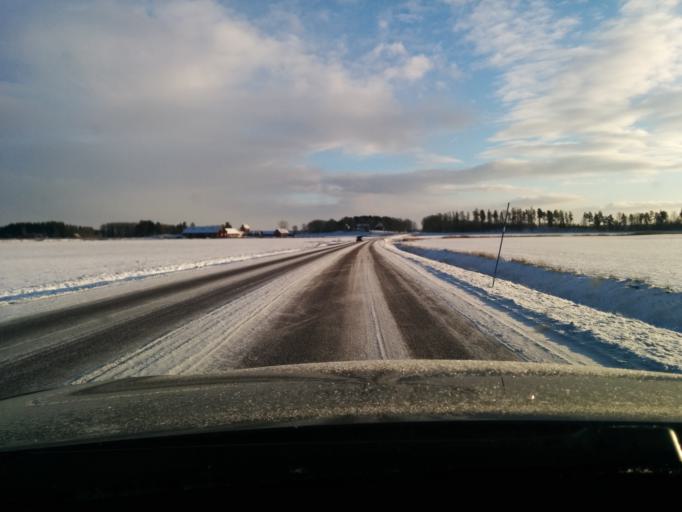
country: SE
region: Uppsala
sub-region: Tierps Kommun
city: Orbyhus
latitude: 60.1804
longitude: 17.6118
